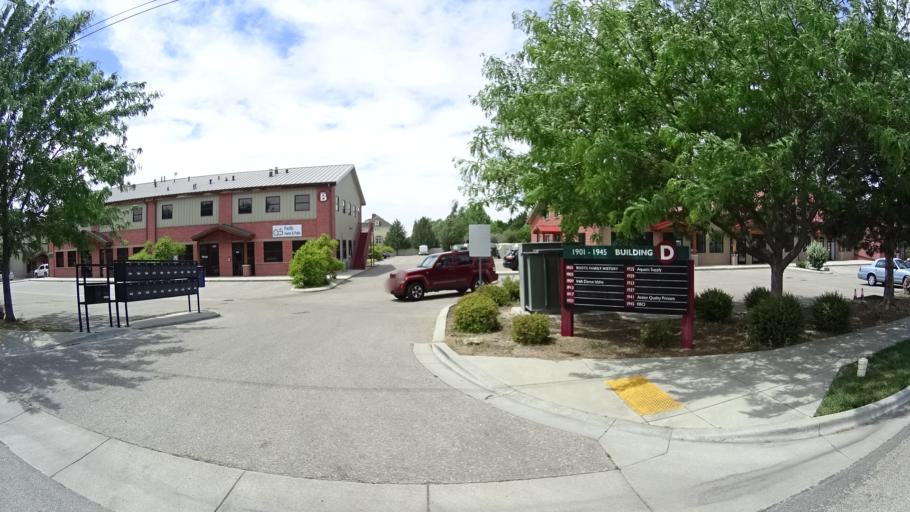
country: US
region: Idaho
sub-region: Ada County
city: Meridian
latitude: 43.6224
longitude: -116.3204
